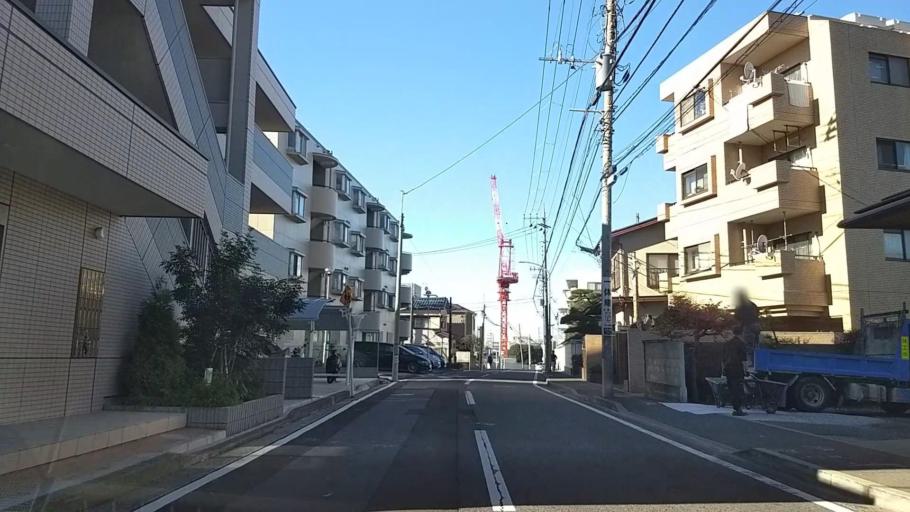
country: JP
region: Kanagawa
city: Yokohama
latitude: 35.4430
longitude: 139.6068
